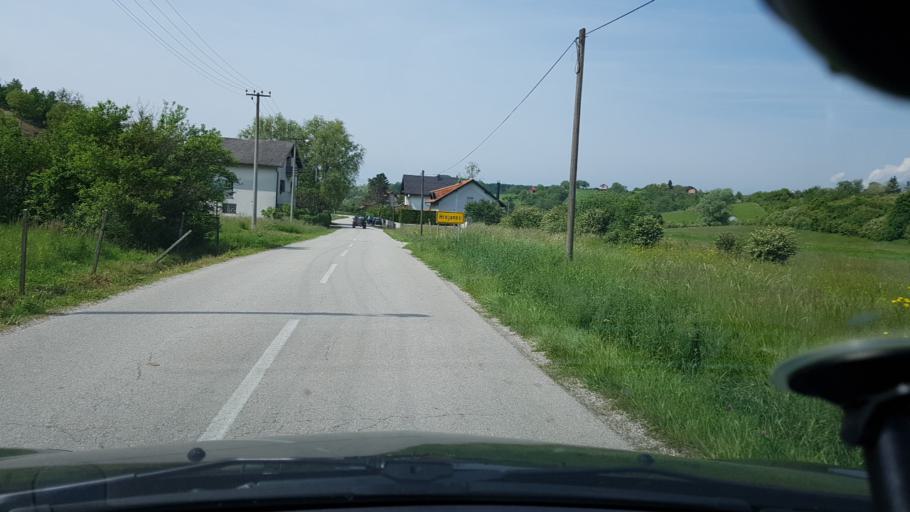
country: HR
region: Krapinsko-Zagorska
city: Marija Bistrica
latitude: 45.9351
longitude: 16.1994
